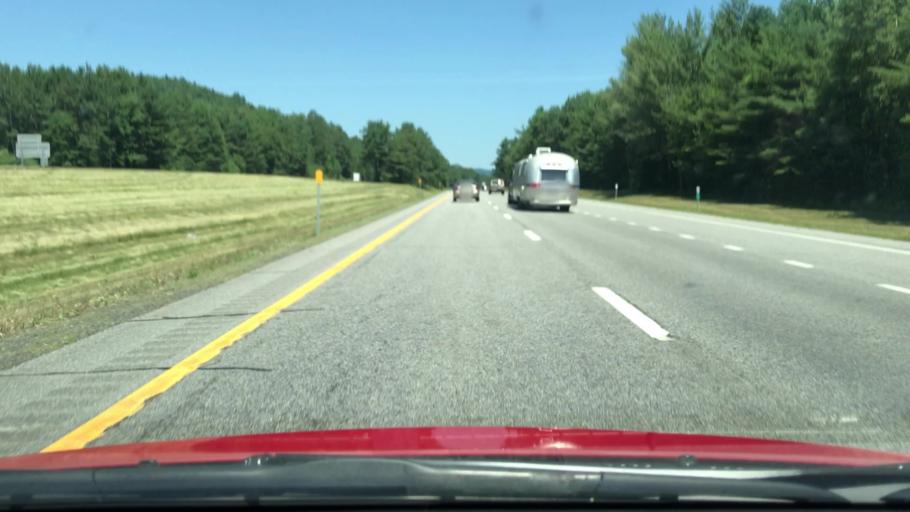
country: US
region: New York
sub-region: Essex County
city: Elizabethtown
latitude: 44.2898
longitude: -73.5317
